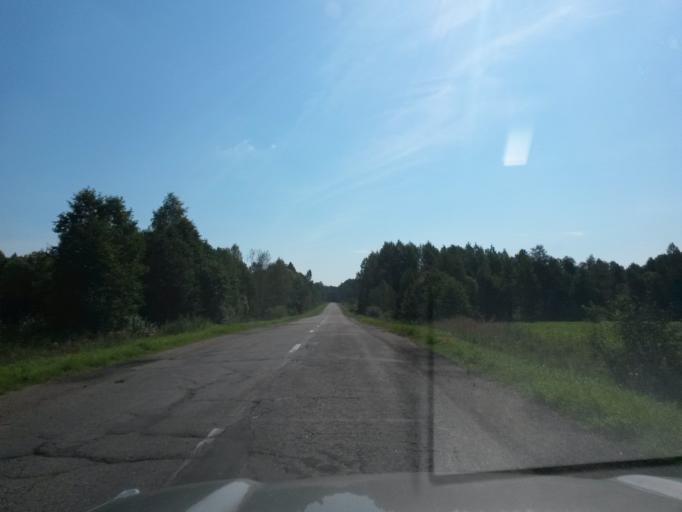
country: RU
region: Jaroslavl
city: Gavrilov-Yam
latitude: 57.3021
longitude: 40.0307
